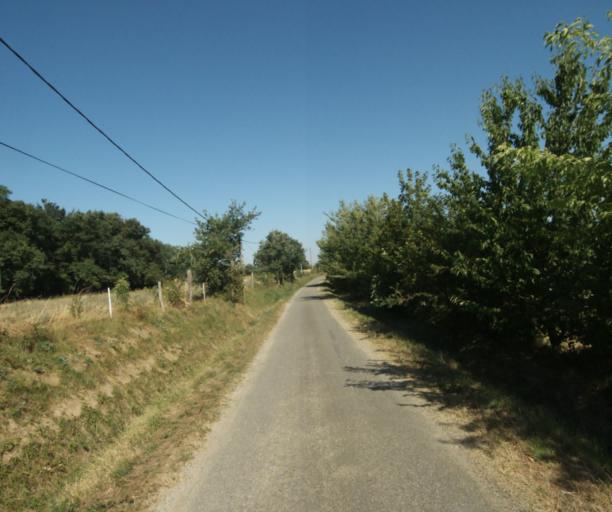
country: FR
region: Midi-Pyrenees
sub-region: Departement de la Haute-Garonne
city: Saint-Felix-Lauragais
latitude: 43.4991
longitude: 1.9255
